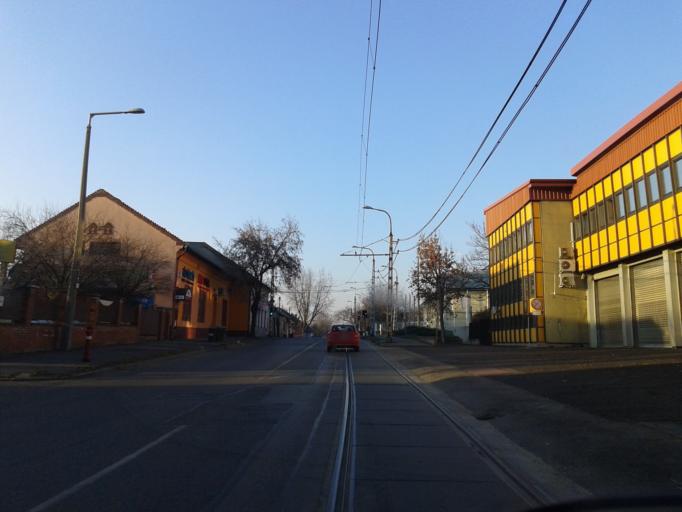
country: HU
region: Budapest
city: Budapest XX. keruelet
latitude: 47.4343
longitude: 19.1066
